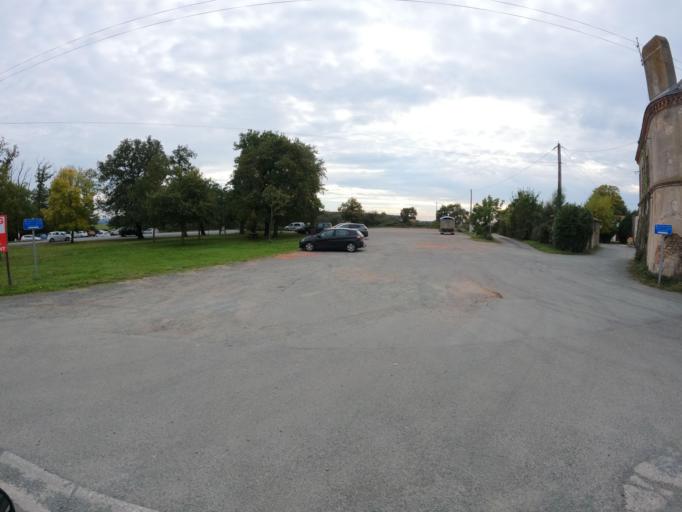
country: FR
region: Pays de la Loire
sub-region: Departement de Maine-et-Loire
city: Torfou
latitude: 47.0321
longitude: -1.0932
